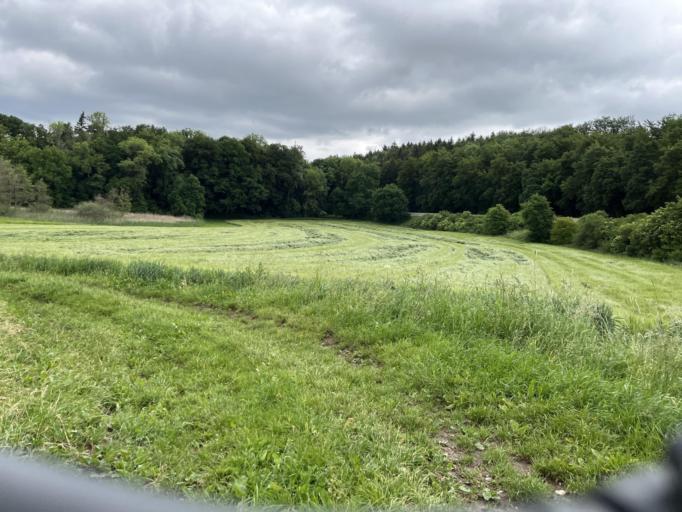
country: DE
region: Baden-Wuerttemberg
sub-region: Tuebingen Region
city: Sigmaringen
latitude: 48.0987
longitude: 9.2400
